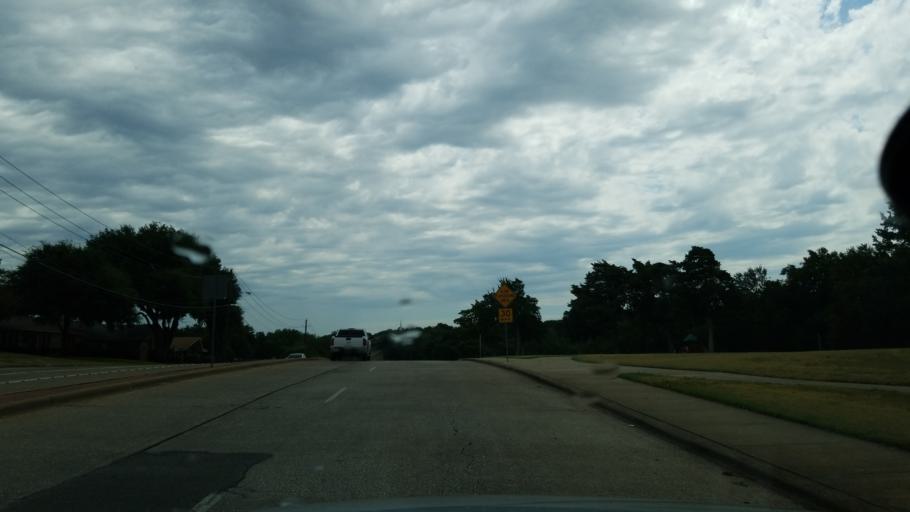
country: US
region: Texas
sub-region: Dallas County
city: Duncanville
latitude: 32.6727
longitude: -96.8398
